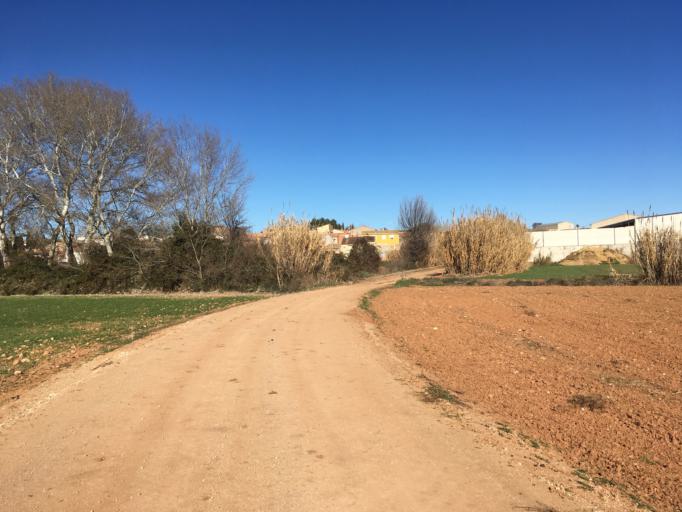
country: ES
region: Castille-La Mancha
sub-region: Provincia de Cuenca
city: Atalaya del Canavate
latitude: 39.5460
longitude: -2.2471
